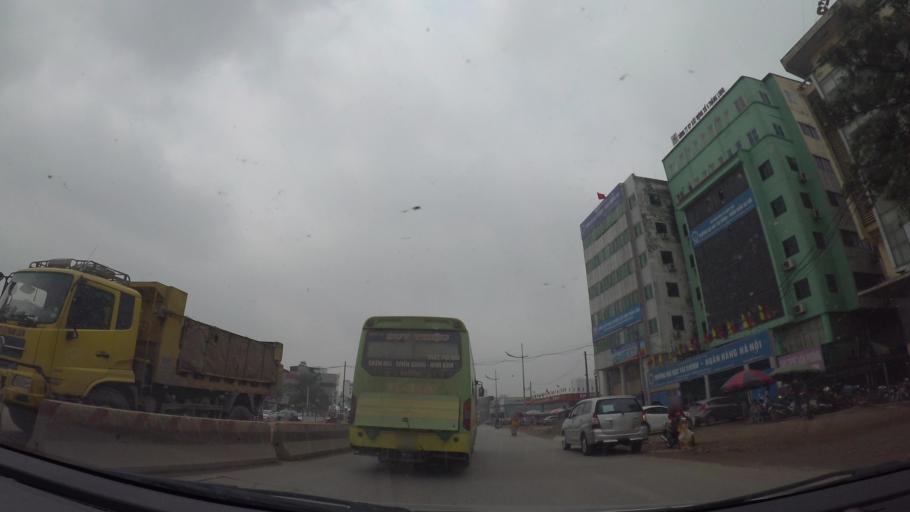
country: VN
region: Ha Noi
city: Tay Ho
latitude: 21.0761
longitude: 105.7859
